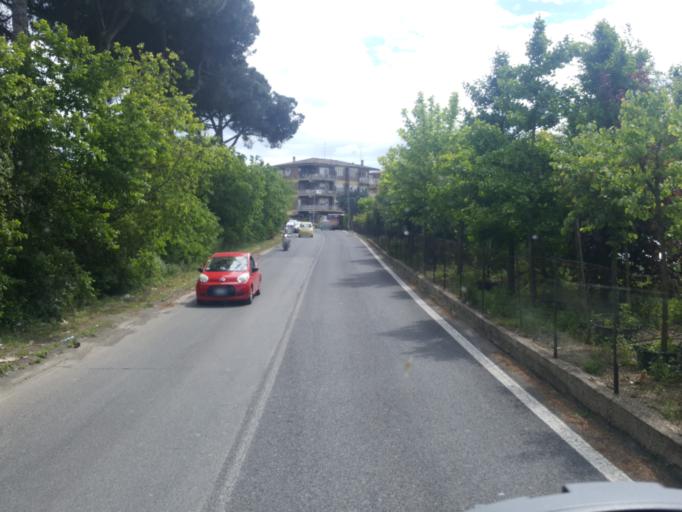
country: IT
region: Latium
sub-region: Citta metropolitana di Roma Capitale
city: La Massimina-Casal Lumbroso
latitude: 41.8849
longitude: 12.3618
